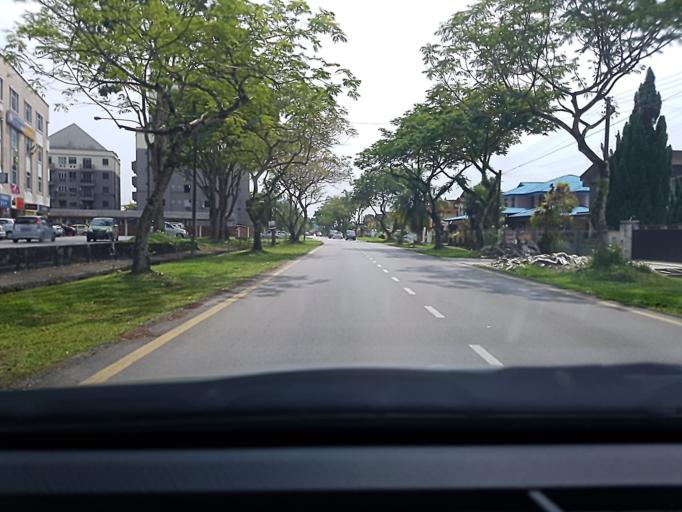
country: MY
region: Sarawak
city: Kuching
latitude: 1.5072
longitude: 110.3625
